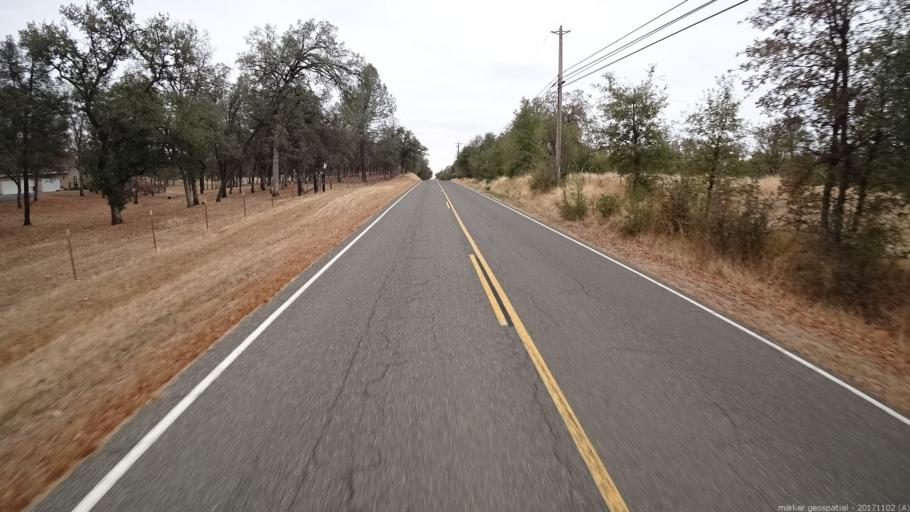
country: US
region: California
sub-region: Shasta County
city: Bella Vista
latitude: 40.6305
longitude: -122.2968
